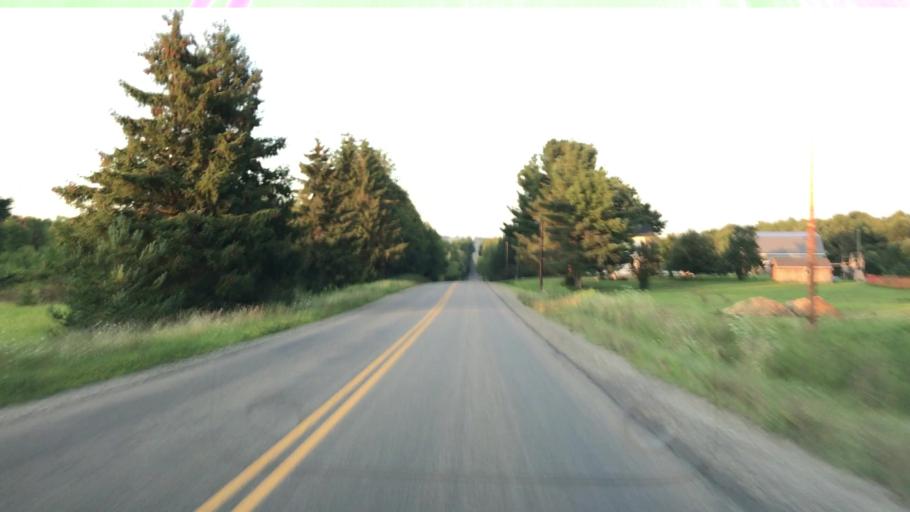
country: US
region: New York
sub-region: Chautauqua County
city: Brocton
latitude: 42.3024
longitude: -79.3926
